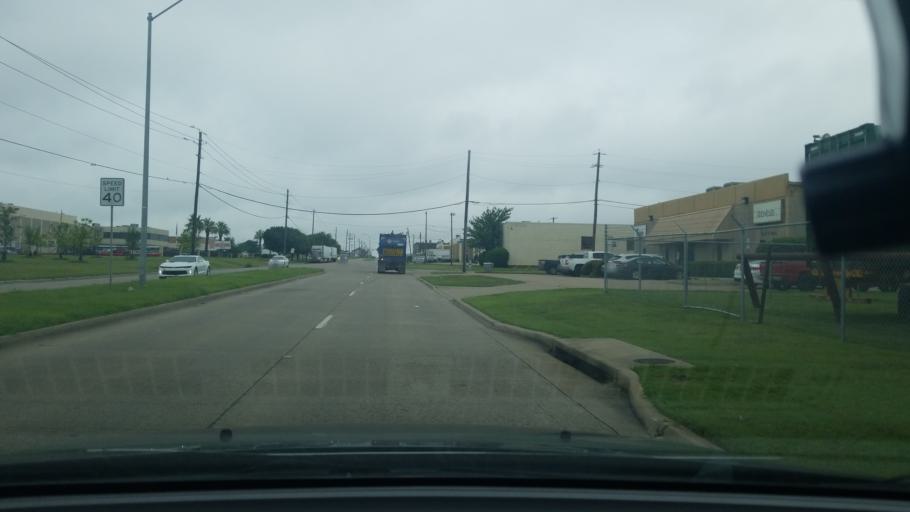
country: US
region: Texas
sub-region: Dallas County
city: Balch Springs
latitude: 32.7781
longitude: -96.6772
